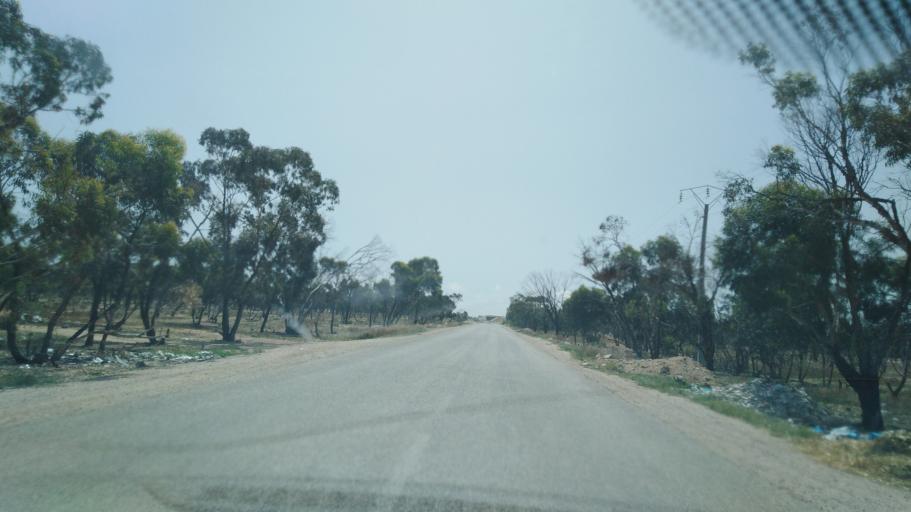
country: TN
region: Safaqis
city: Sfax
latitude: 34.7232
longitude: 10.5755
